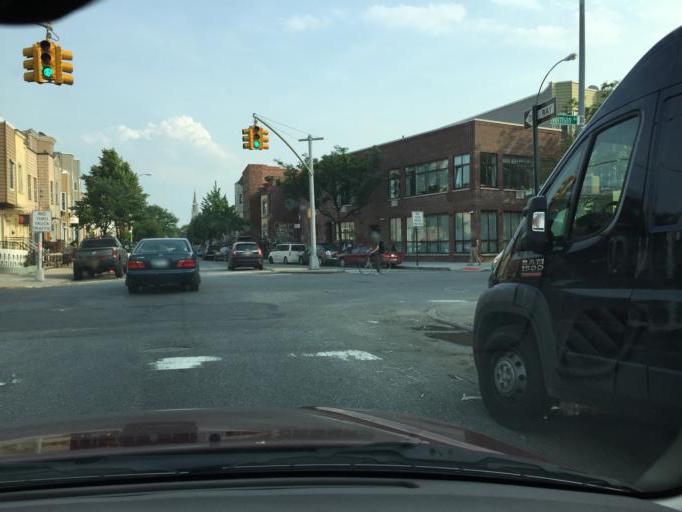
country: US
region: New York
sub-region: Queens County
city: Long Island City
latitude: 40.7275
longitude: -73.9458
